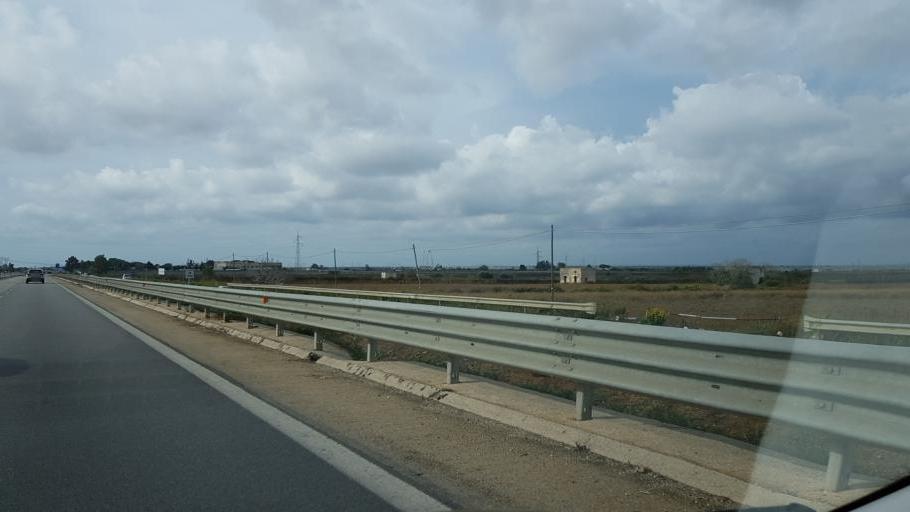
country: IT
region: Apulia
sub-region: Provincia di Brindisi
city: Brindisi
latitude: 40.6125
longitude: 17.8964
